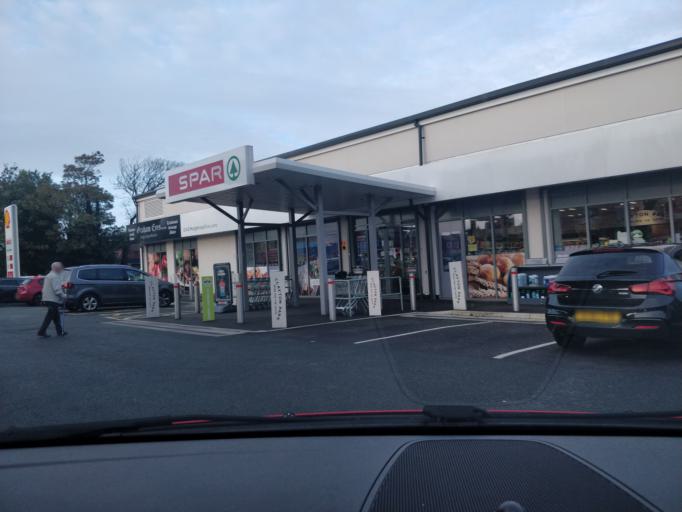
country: GB
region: England
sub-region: Sefton
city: Southport
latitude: 53.6500
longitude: -2.9855
